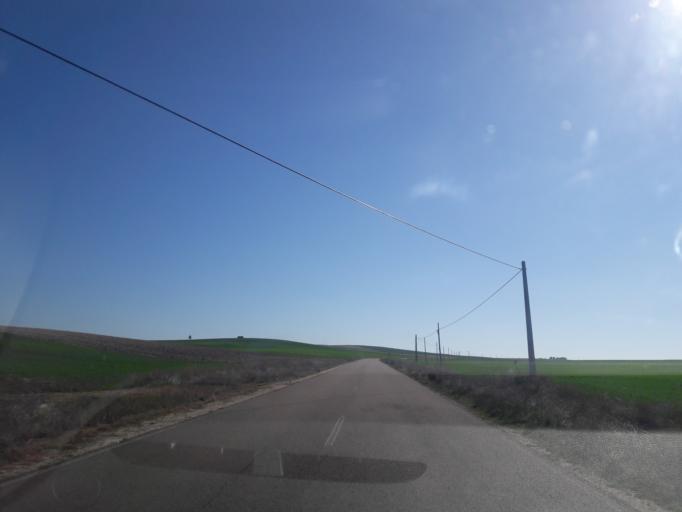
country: ES
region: Castille and Leon
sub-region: Provincia de Salamanca
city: Tordillos
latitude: 40.8511
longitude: -5.3325
